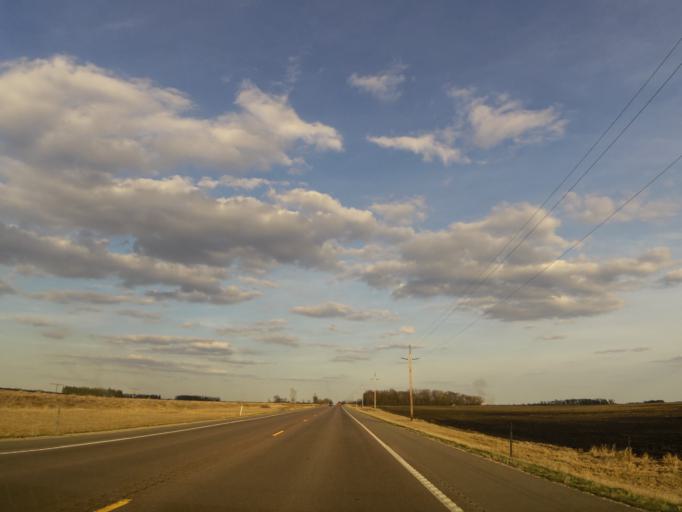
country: US
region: Minnesota
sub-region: Renville County
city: Hector
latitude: 44.7250
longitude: -94.5497
